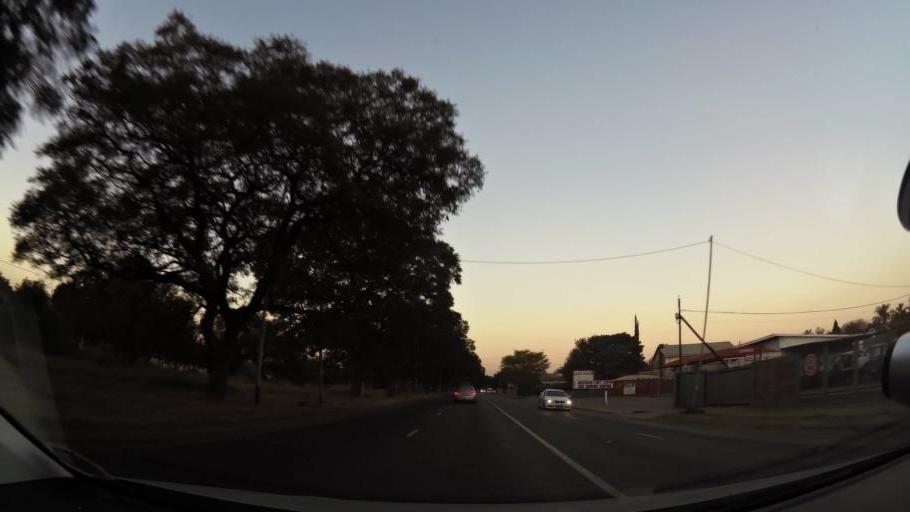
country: ZA
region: Gauteng
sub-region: City of Tshwane Metropolitan Municipality
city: Pretoria
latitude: -25.7179
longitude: 28.1451
